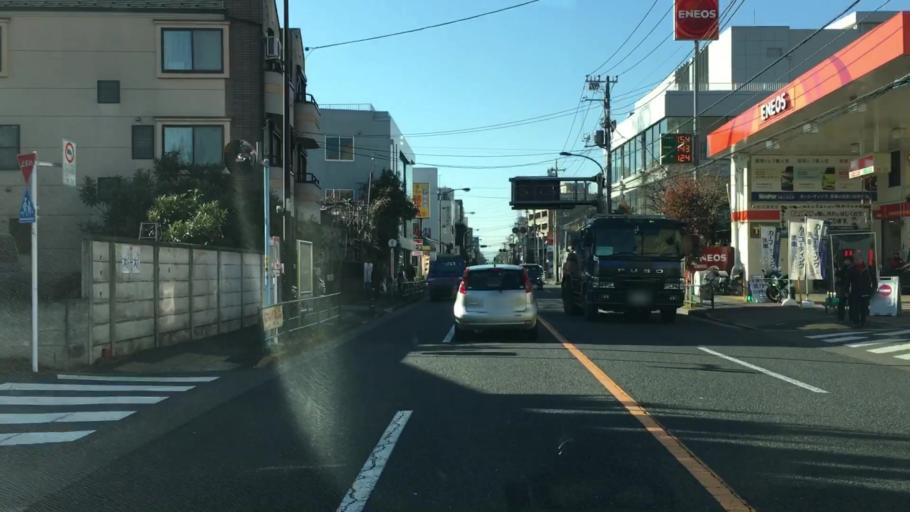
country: JP
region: Tokyo
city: Mitaka-shi
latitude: 35.6899
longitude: 139.6131
